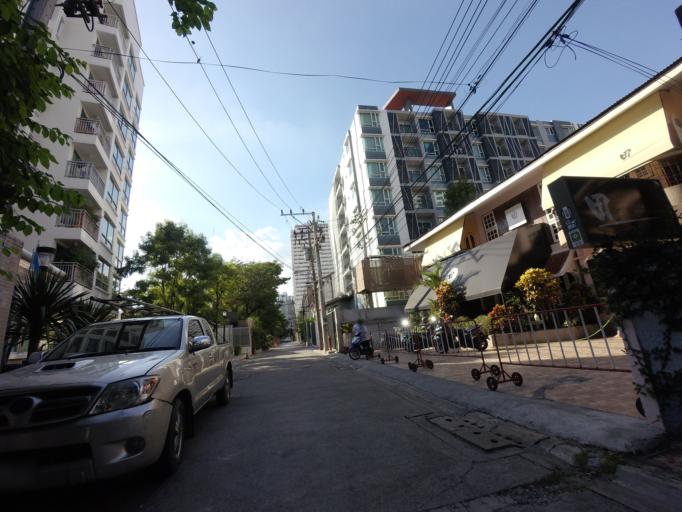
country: TH
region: Bangkok
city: Watthana
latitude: 13.7302
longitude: 100.5774
